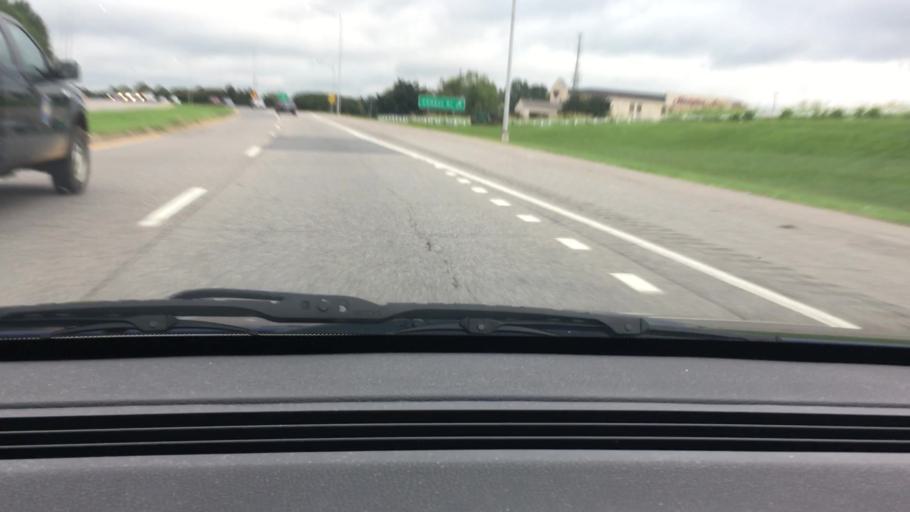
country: US
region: Alabama
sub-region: Tuscaloosa County
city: Tuscaloosa
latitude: 33.2101
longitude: -87.5245
